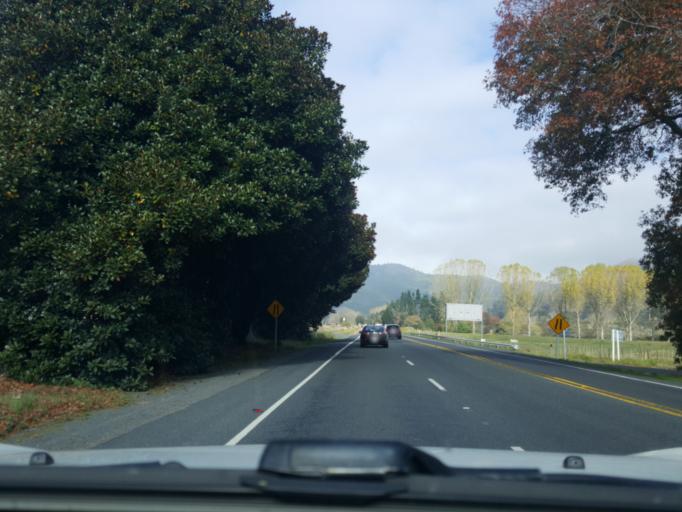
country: NZ
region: Waikato
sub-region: Waikato District
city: Ngaruawahia
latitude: -37.5856
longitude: 175.1595
